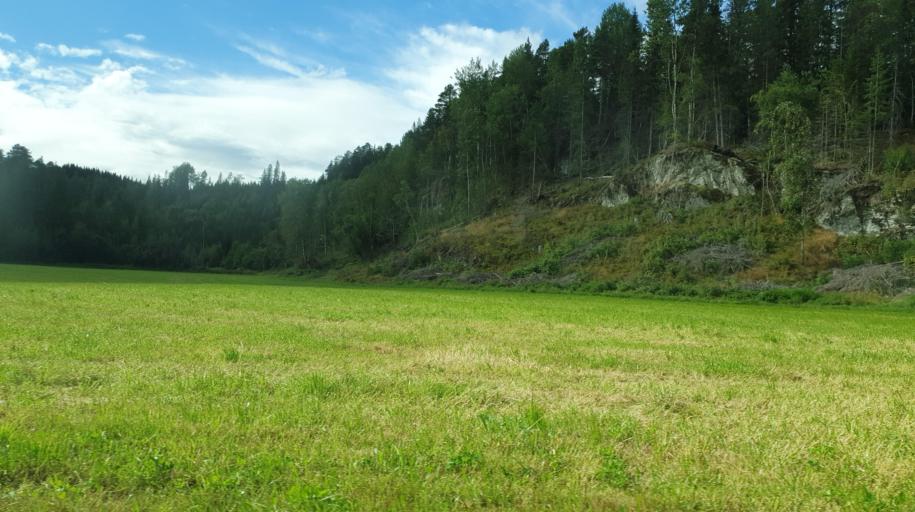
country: NO
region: Nord-Trondelag
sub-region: Levanger
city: Skogn
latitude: 63.5964
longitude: 11.2676
